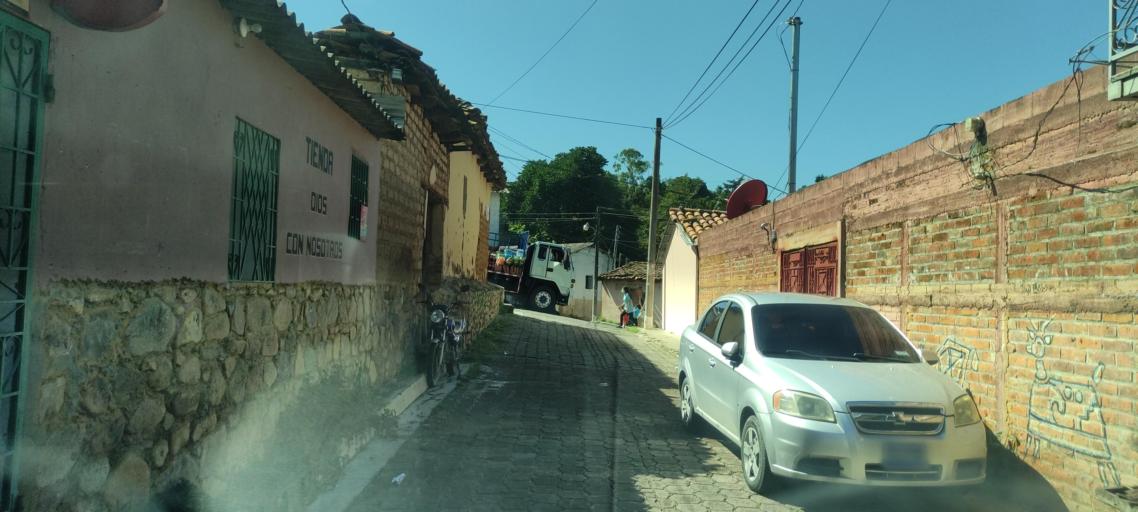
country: HN
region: Ocotepeque
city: Antigua Ocotepeque
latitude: 14.3170
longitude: -89.1717
